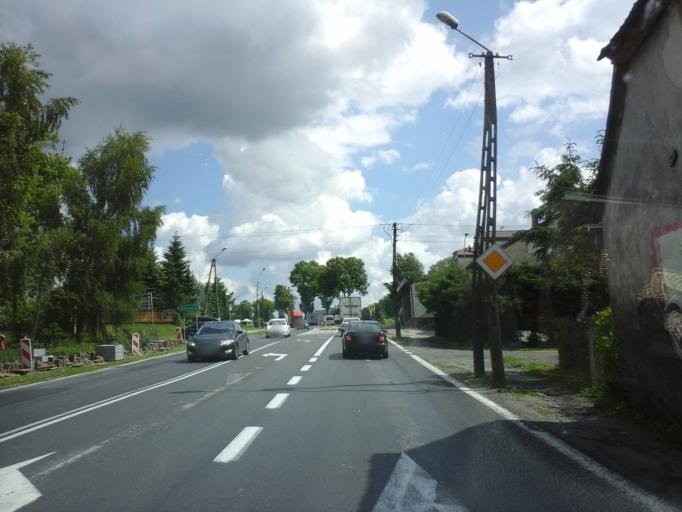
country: PL
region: West Pomeranian Voivodeship
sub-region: Powiat koszalinski
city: Mielno
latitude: 54.1322
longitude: 16.0372
